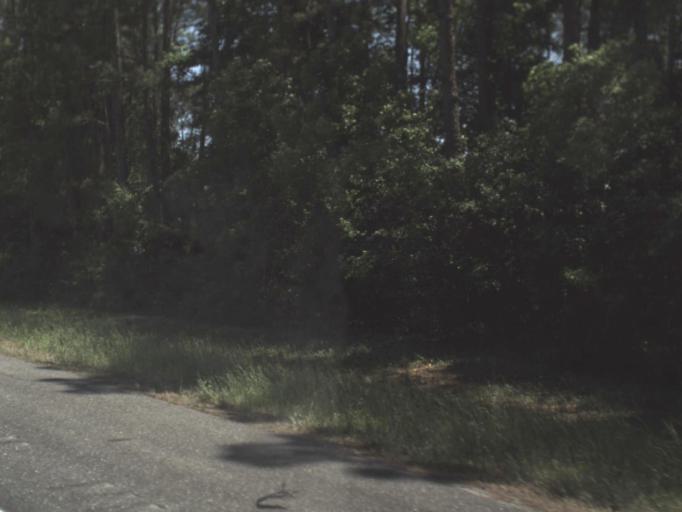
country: US
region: Florida
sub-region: Jefferson County
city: Monticello
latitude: 30.4784
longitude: -83.9277
